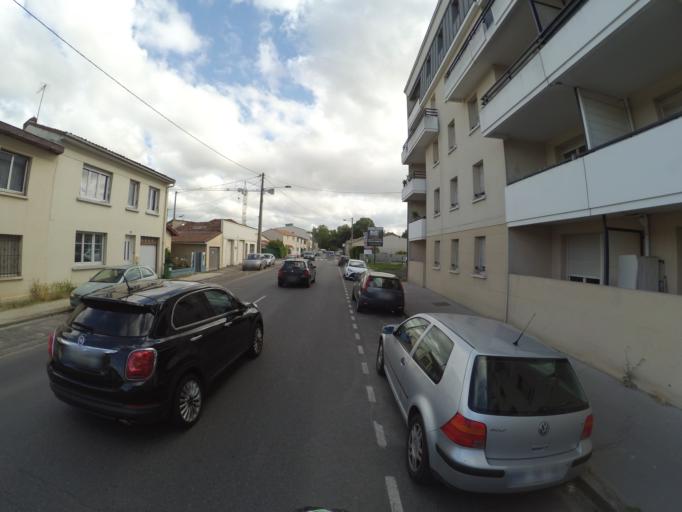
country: FR
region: Aquitaine
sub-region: Departement de la Gironde
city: Lormont
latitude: 44.8775
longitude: -0.5528
